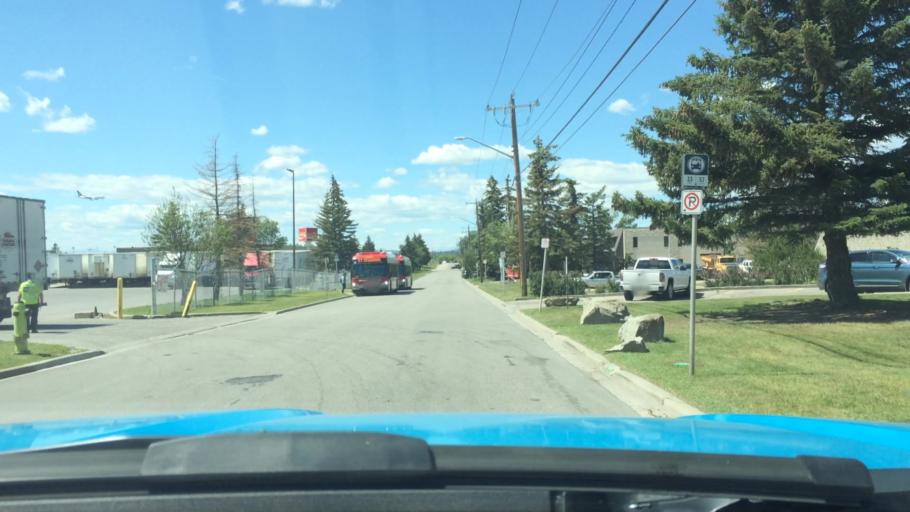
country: CA
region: Alberta
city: Calgary
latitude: 51.0883
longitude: -114.0064
